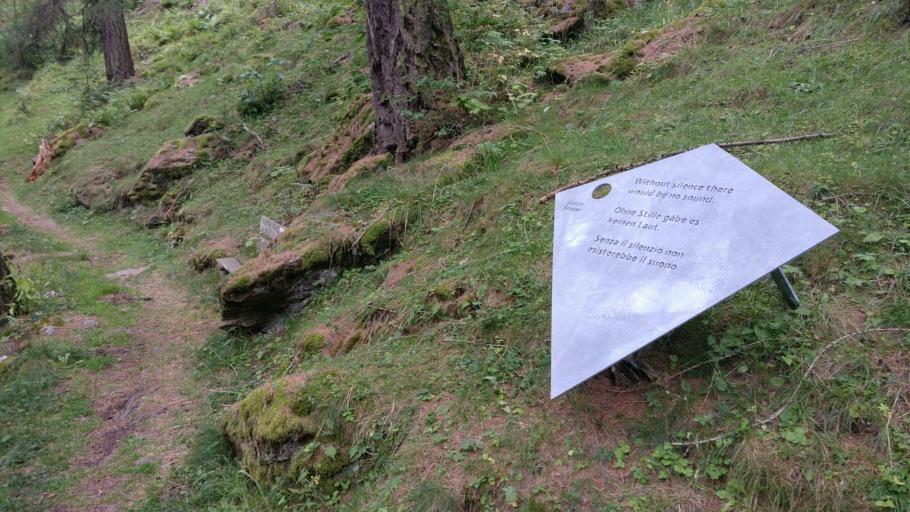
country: IT
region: Trentino-Alto Adige
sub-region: Bolzano
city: Senales
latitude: 46.7122
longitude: 10.8910
